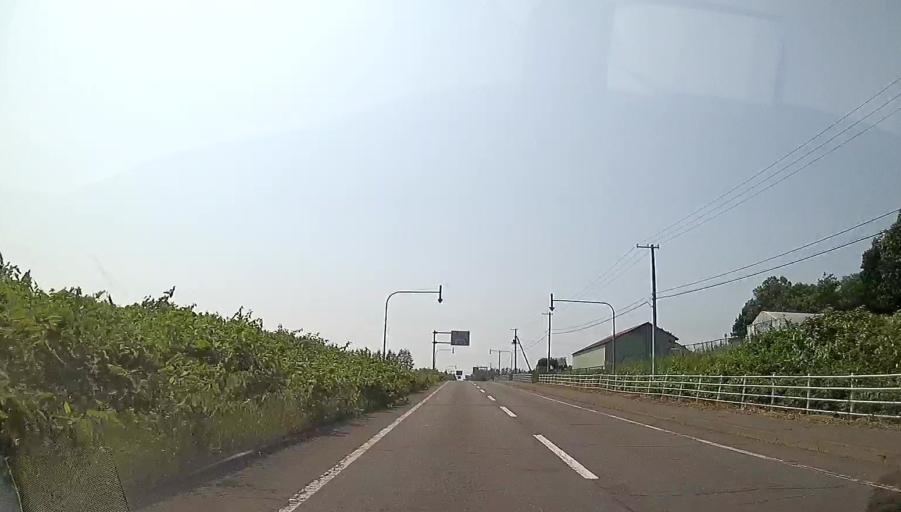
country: JP
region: Hokkaido
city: Otofuke
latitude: 43.1696
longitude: 143.1148
